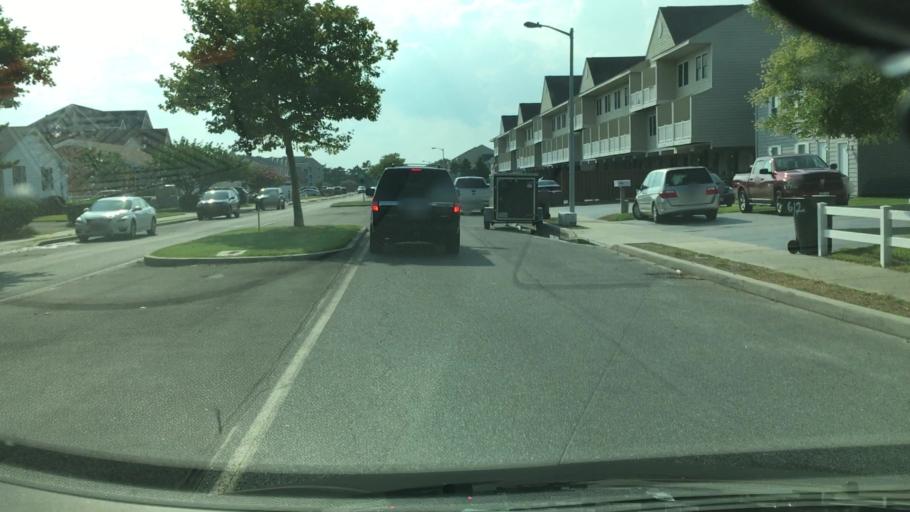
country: US
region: Maryland
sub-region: Worcester County
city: Ocean City
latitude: 38.4098
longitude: -75.0635
